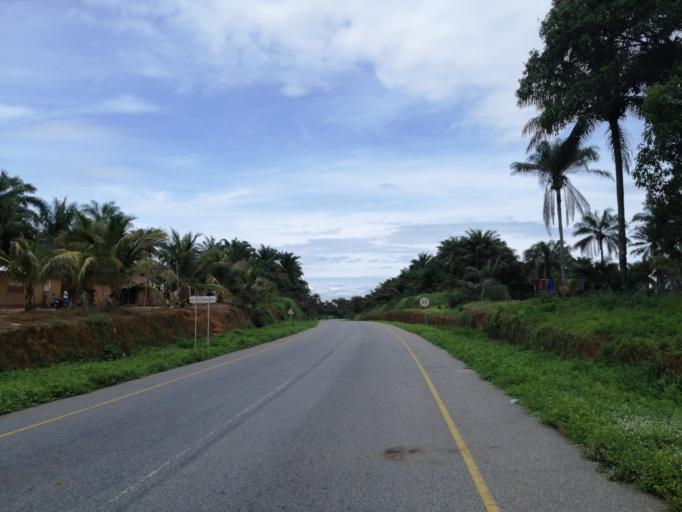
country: SL
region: Northern Province
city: Port Loko
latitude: 8.7620
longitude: -12.9091
